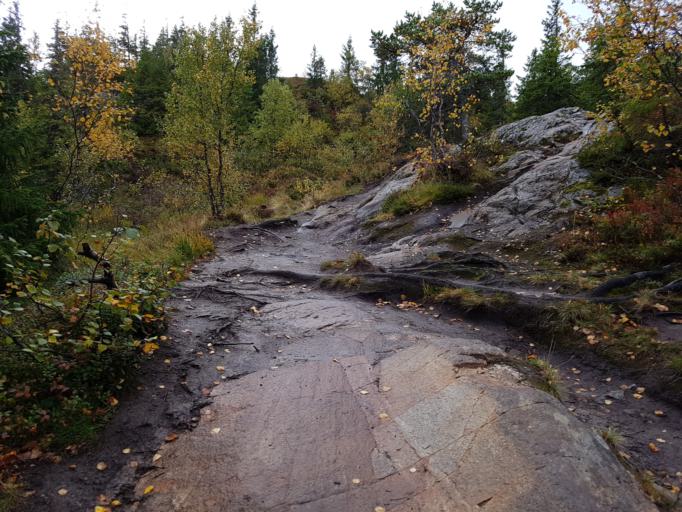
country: NO
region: Sor-Trondelag
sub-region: Melhus
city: Melhus
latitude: 63.4049
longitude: 10.2035
